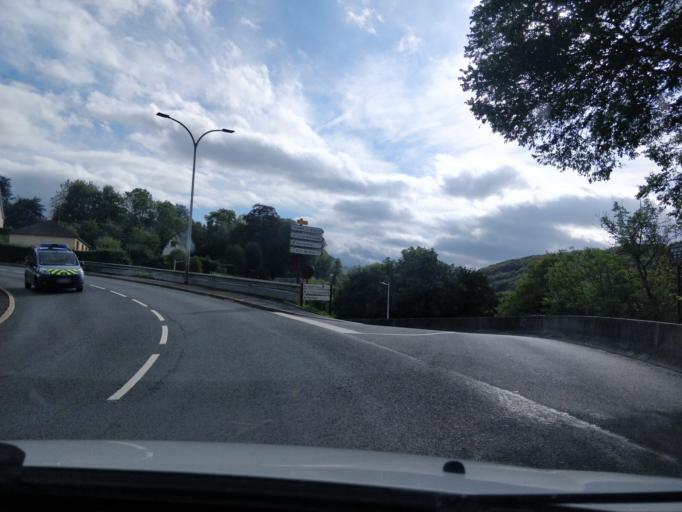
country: FR
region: Lower Normandy
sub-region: Departement du Calvados
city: Vire
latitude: 48.8429
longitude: -0.8995
